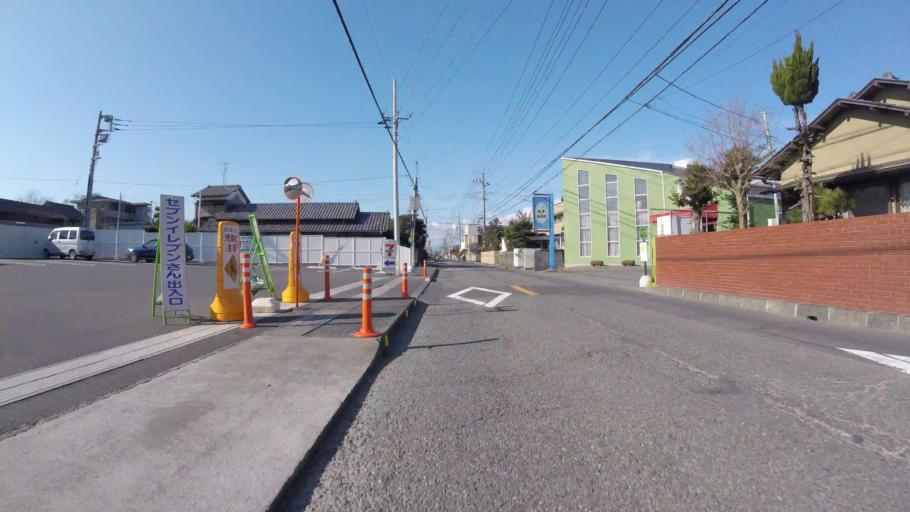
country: JP
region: Shizuoka
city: Numazu
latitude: 35.1072
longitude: 138.8355
